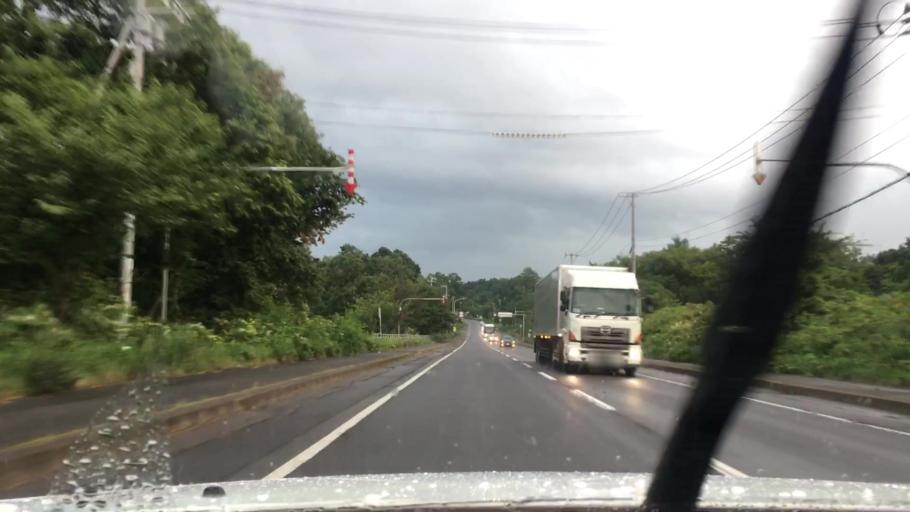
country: JP
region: Hokkaido
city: Nanae
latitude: 42.0867
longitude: 140.5836
